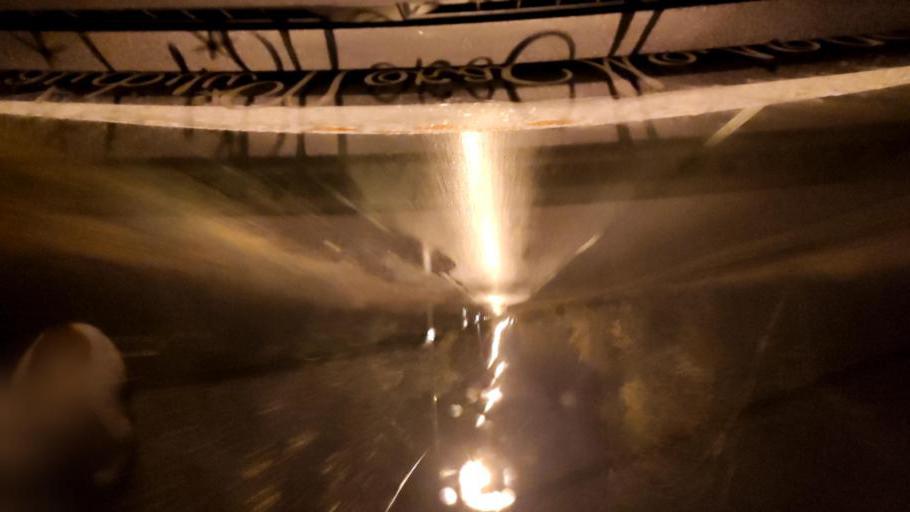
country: RU
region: Voronezj
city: Somovo
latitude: 51.7067
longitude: 39.3252
